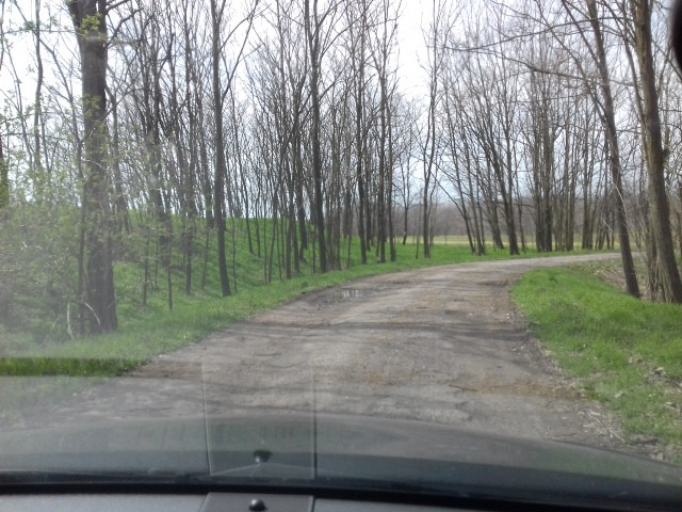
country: HU
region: Bacs-Kiskun
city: Tiszakecske
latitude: 46.9017
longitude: 20.1378
